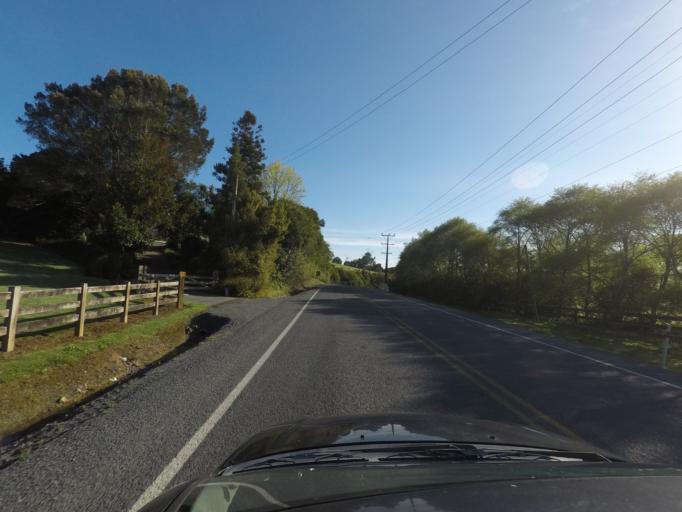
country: NZ
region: Auckland
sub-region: Auckland
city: Red Hill
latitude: -36.9934
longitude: 174.9848
